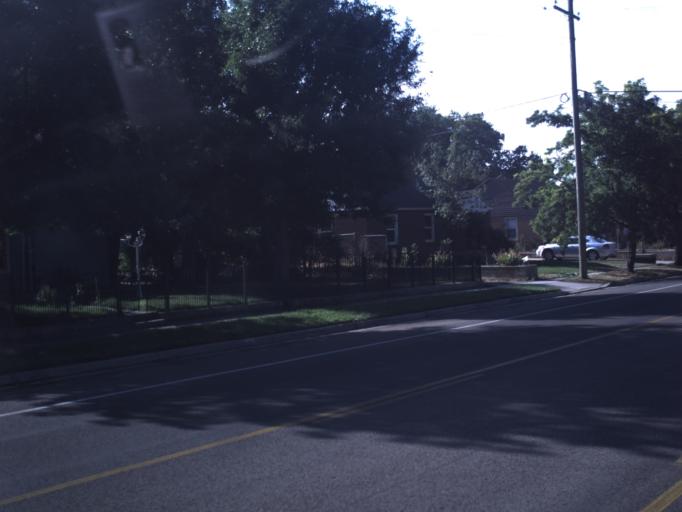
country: US
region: Utah
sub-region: Utah County
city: American Fork
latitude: 40.3863
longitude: -111.7959
